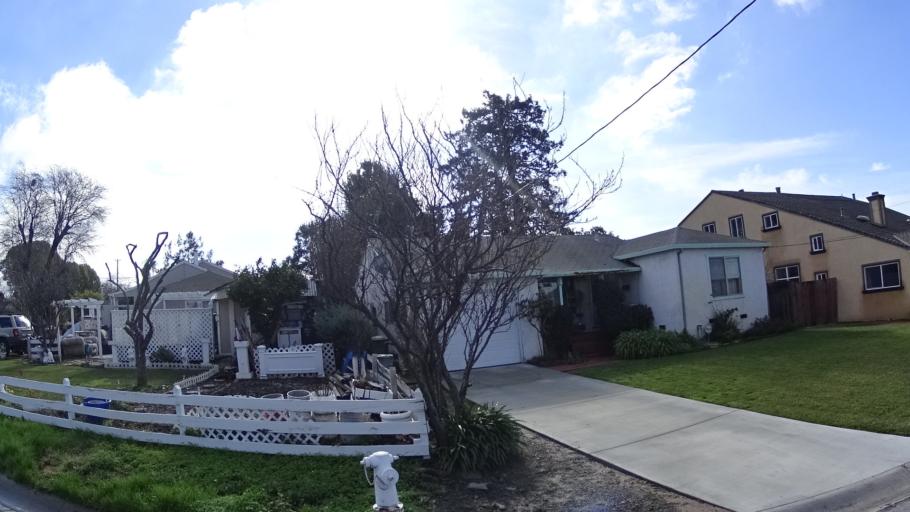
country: US
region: California
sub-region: Alameda County
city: Castro Valley
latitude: 37.6898
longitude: -122.0686
